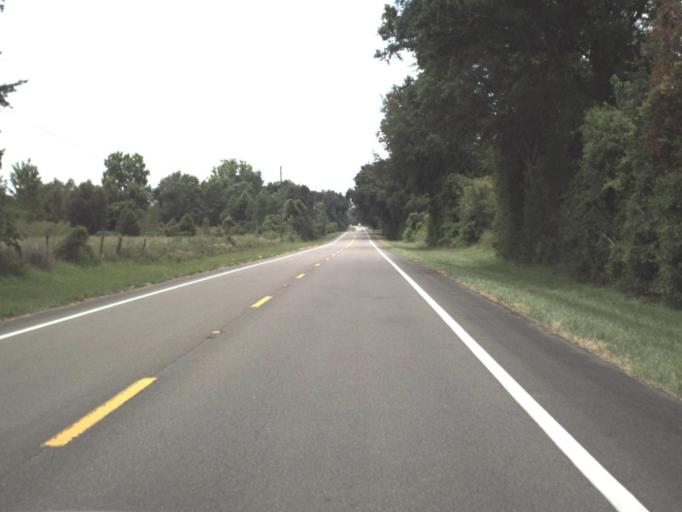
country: US
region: Florida
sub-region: Alachua County
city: Archer
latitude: 29.4966
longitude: -82.4957
